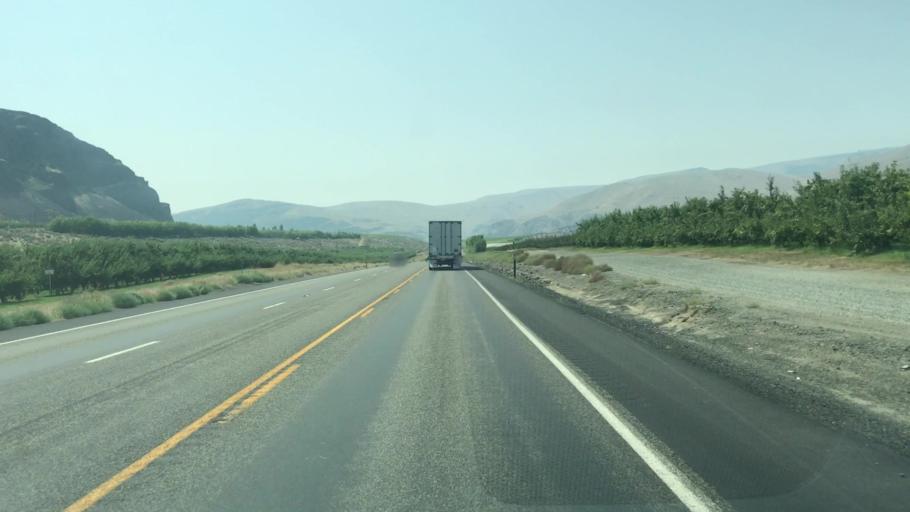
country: US
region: Washington
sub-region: Grant County
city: Quincy
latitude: 47.2707
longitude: -120.0698
